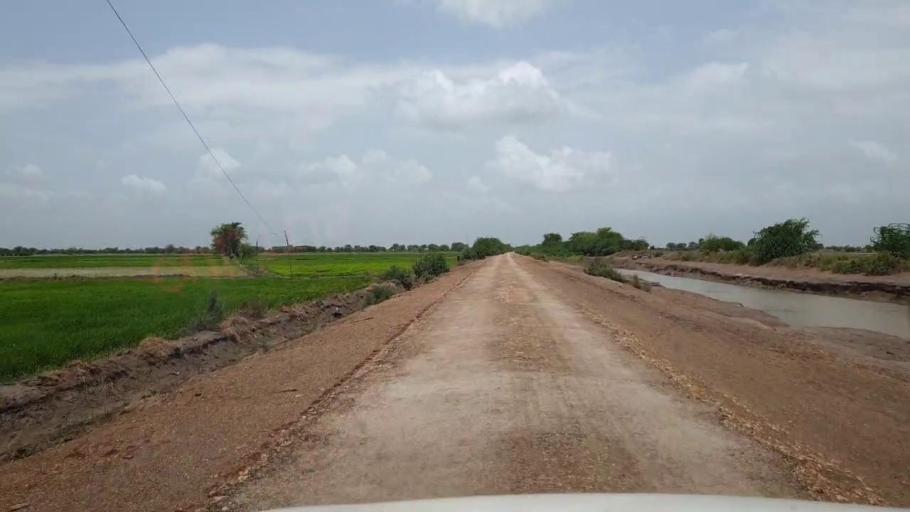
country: PK
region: Sindh
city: Kario
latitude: 24.7162
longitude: 68.5835
